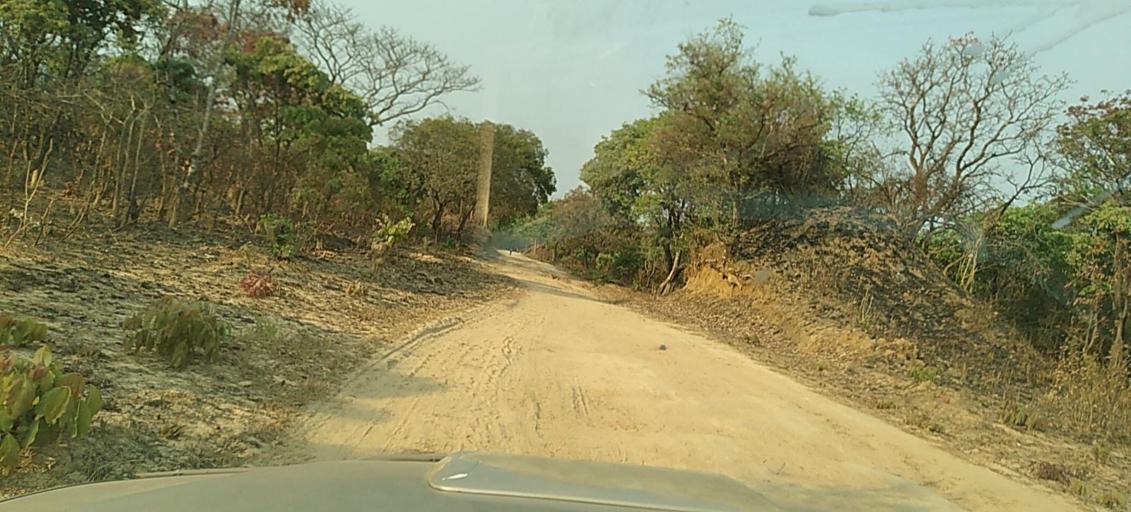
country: ZM
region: North-Western
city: Kasempa
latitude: -13.2685
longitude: 26.5601
